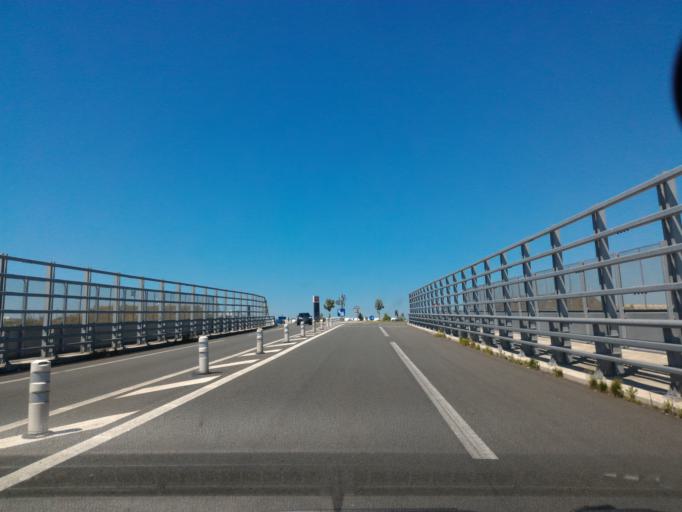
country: FR
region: Poitou-Charentes
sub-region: Departement de la Vienne
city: Jaunay-Clan
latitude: 46.7019
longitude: 0.3693
